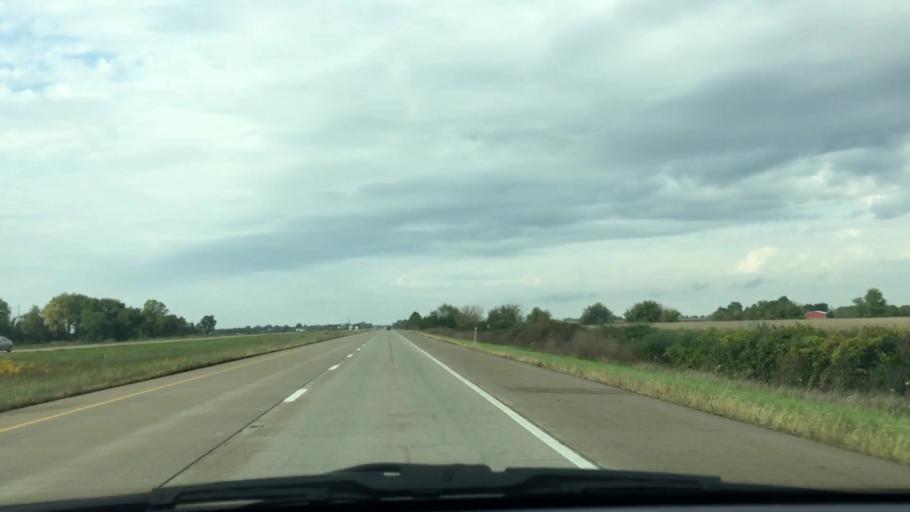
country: US
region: Illinois
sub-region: Whiteside County
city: Prophetstown
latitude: 41.7499
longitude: -89.8665
